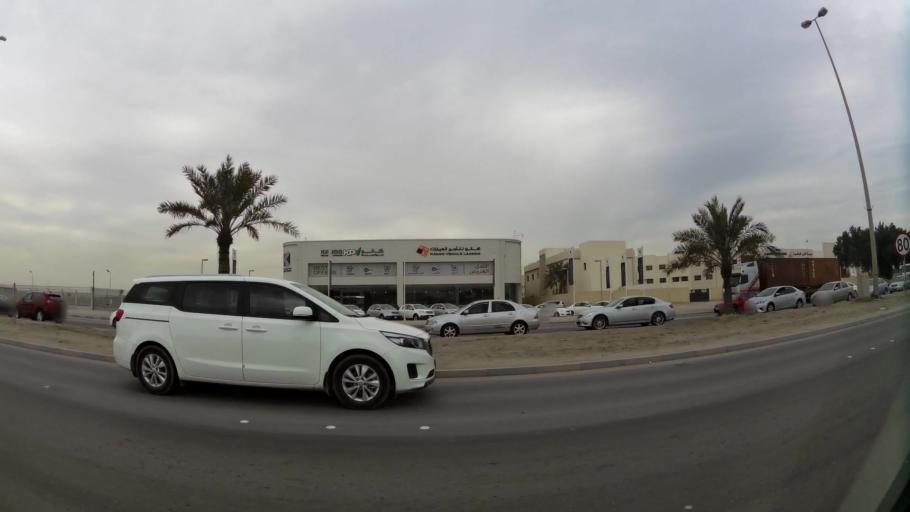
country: BH
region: Northern
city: Sitrah
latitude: 26.1657
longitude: 50.6041
